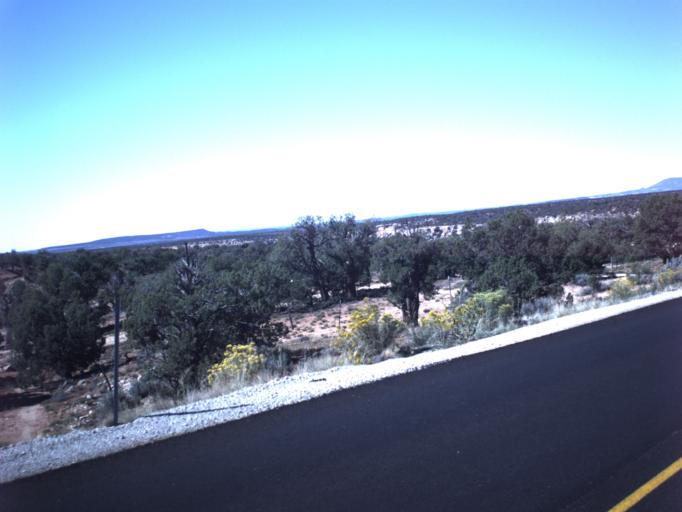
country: US
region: Utah
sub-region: San Juan County
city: Blanding
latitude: 37.5742
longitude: -109.5009
